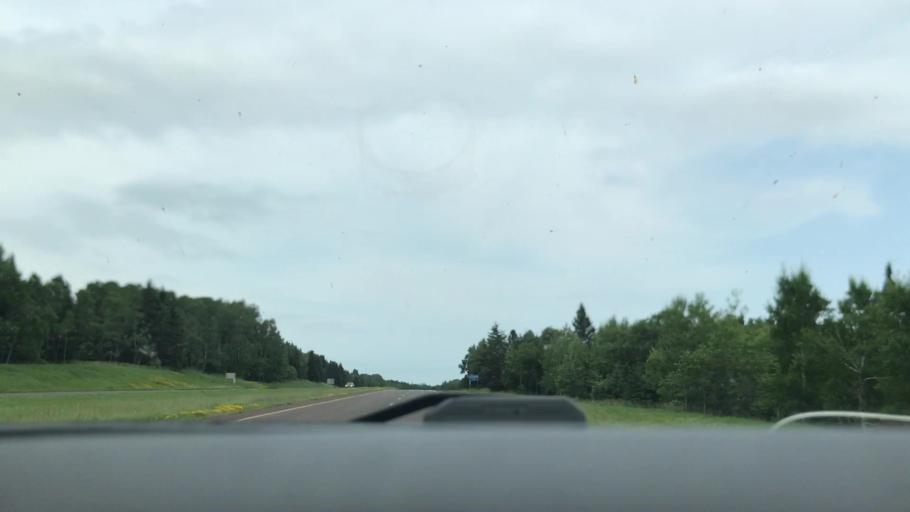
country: US
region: Minnesota
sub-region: Lake County
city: Two Harbors
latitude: 47.0123
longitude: -91.7082
